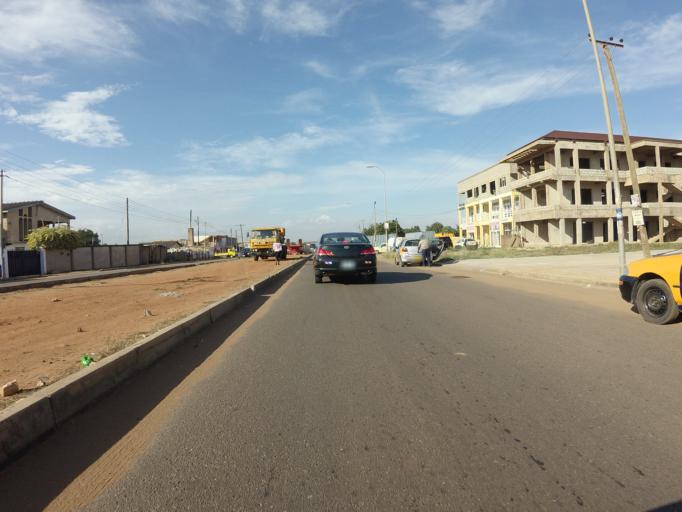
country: GH
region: Greater Accra
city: Nungua
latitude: 5.6446
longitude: -0.0594
